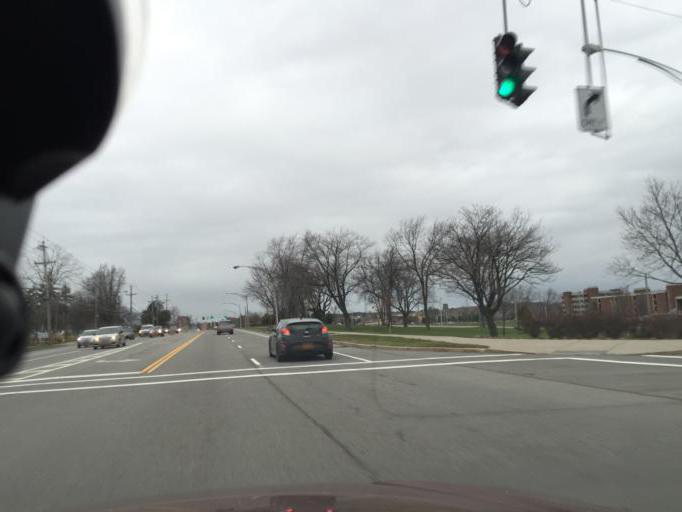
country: US
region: New York
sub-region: Monroe County
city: Rochester
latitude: 43.0981
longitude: -77.6133
